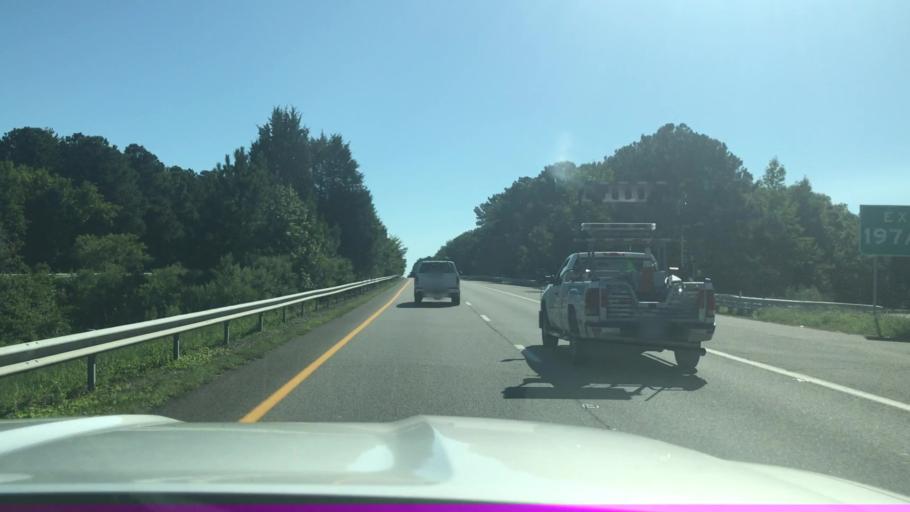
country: US
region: Virginia
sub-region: Henrico County
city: Highland Springs
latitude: 37.5299
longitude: -77.3310
